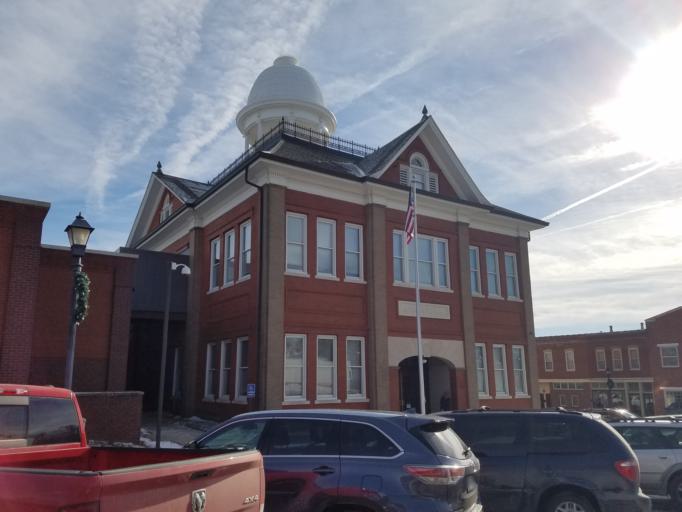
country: US
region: Missouri
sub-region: Lafayette County
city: Lexington
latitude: 39.1848
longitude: -93.8833
